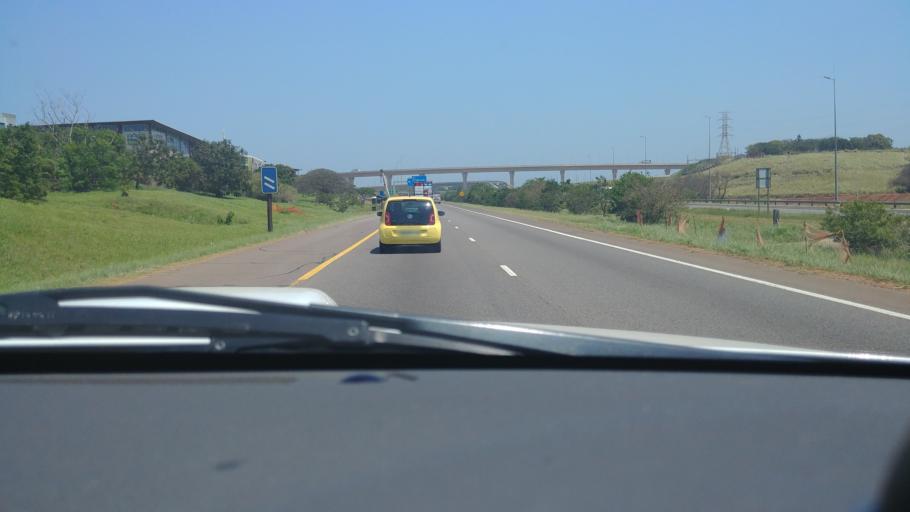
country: ZA
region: KwaZulu-Natal
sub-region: eThekwini Metropolitan Municipality
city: Durban
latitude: -29.7162
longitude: 31.0630
